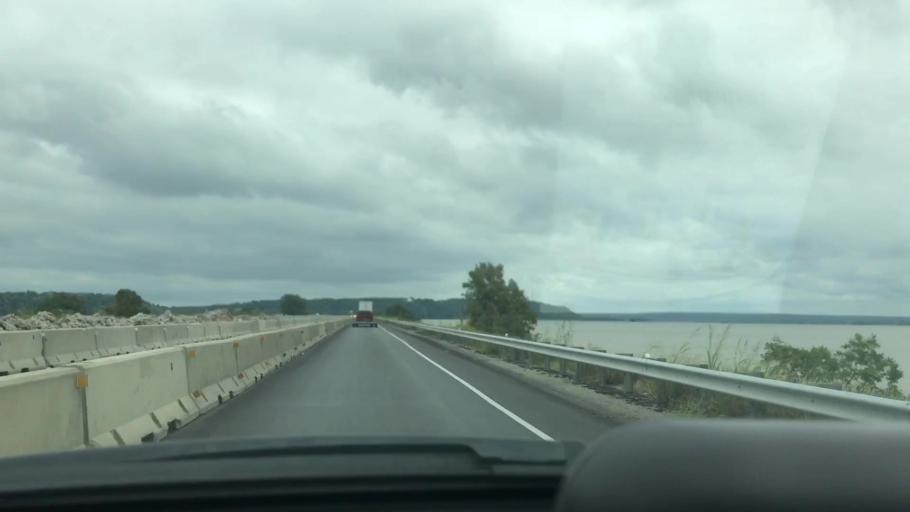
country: US
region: Oklahoma
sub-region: McIntosh County
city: Eufaula
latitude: 35.2305
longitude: -95.5977
